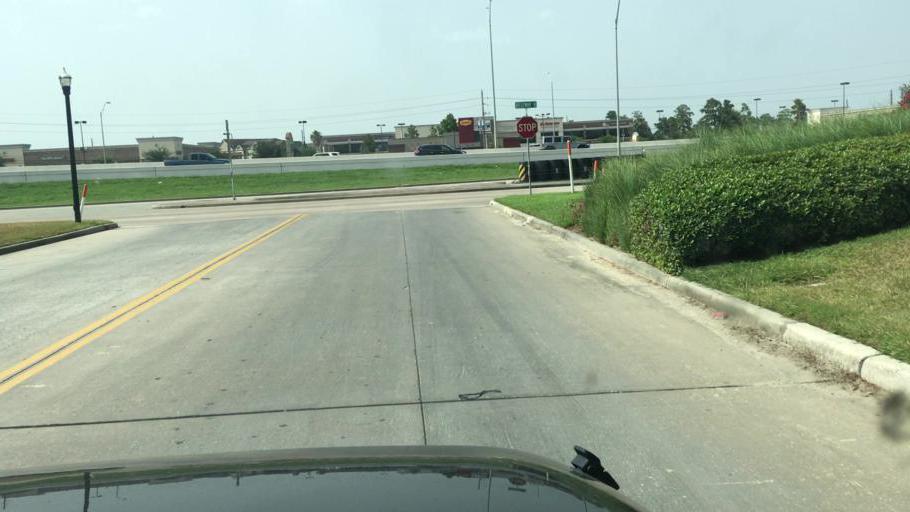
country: US
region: Texas
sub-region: Harris County
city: Humble
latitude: 29.9339
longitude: -95.2459
